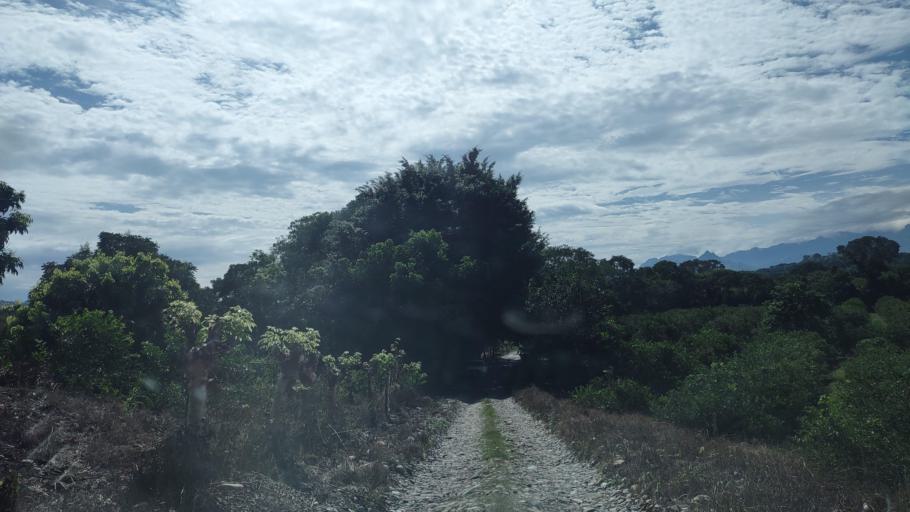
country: MX
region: Veracruz
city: Santa Cruz Hidalgo
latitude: 19.9957
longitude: -96.9603
